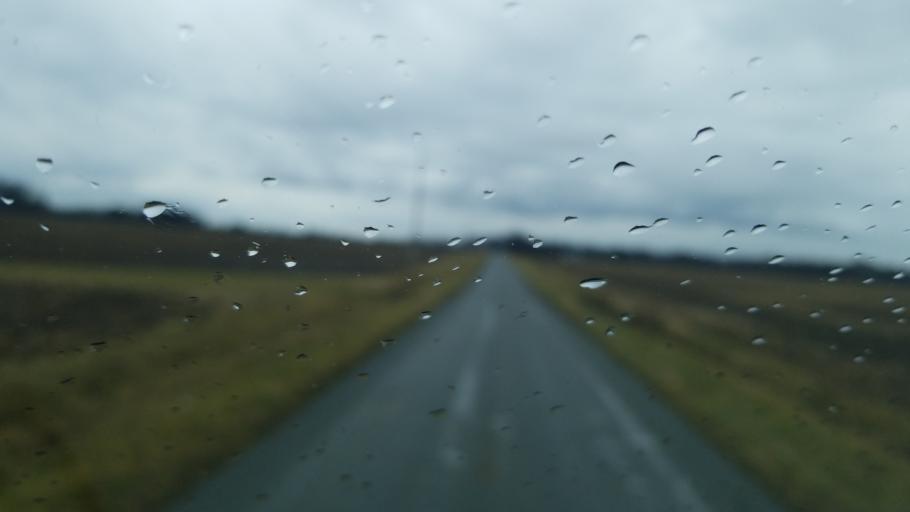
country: US
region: Ohio
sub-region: Hardin County
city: Forest
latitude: 40.7521
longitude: -83.4002
